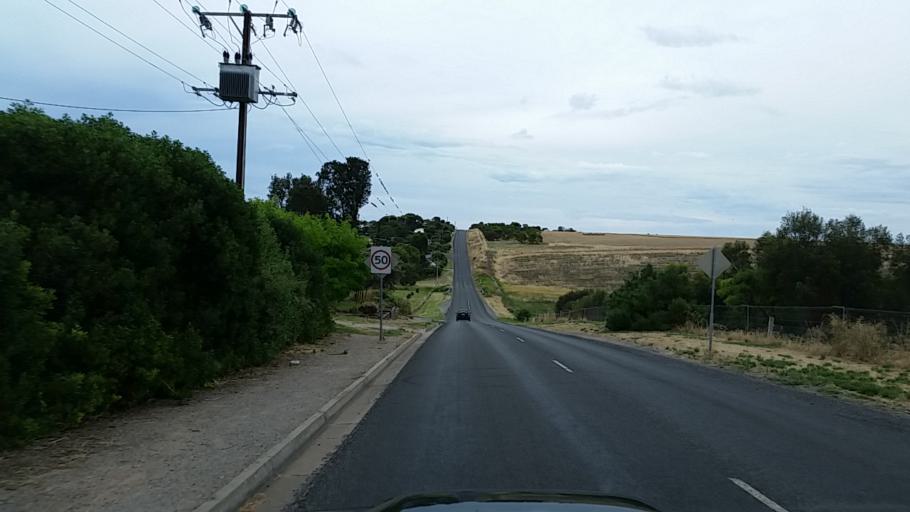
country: AU
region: South Australia
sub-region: Onkaparinga
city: Port Willunga
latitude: -35.2634
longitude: 138.4700
